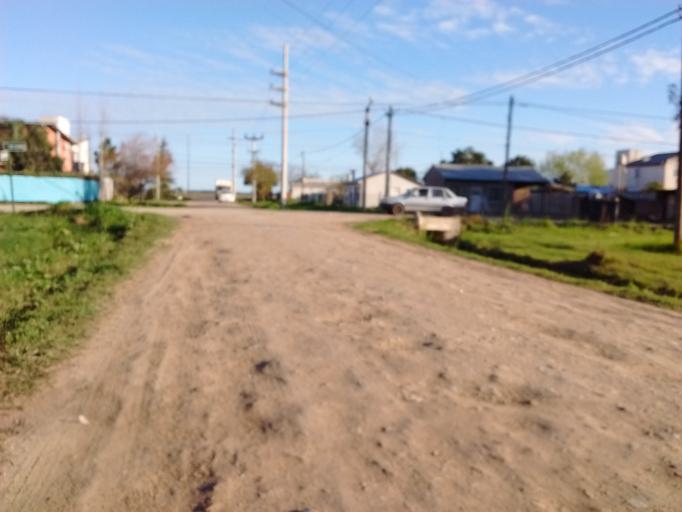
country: AR
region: Santa Fe
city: Funes
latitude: -32.9275
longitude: -60.7935
